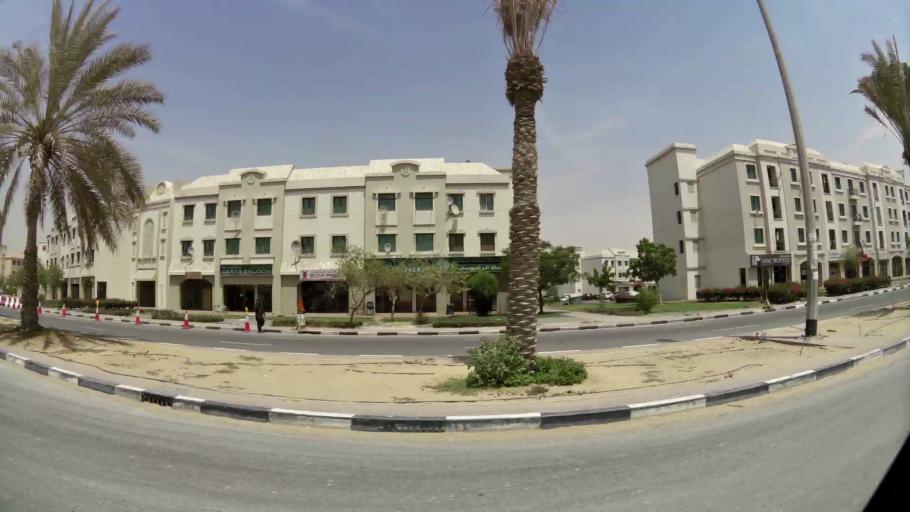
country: AE
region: Ash Shariqah
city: Sharjah
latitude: 25.1731
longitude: 55.3992
